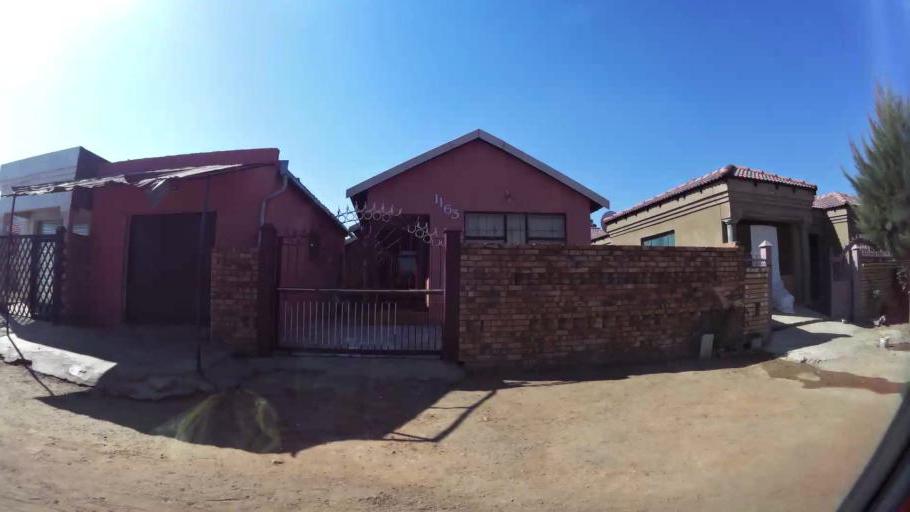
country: ZA
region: Gauteng
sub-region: City of Tshwane Metropolitan Municipality
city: Mabopane
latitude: -25.5597
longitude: 28.0818
